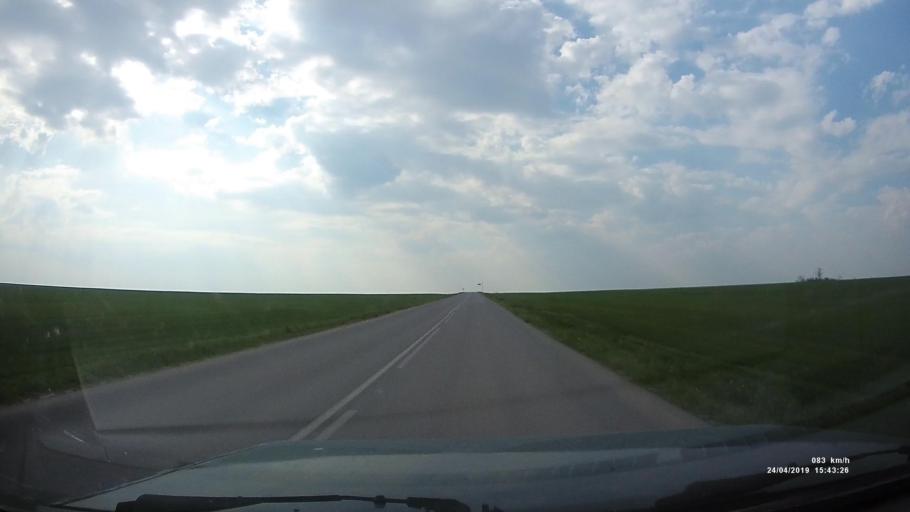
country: RU
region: Kalmykiya
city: Yashalta
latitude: 46.5827
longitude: 42.7725
